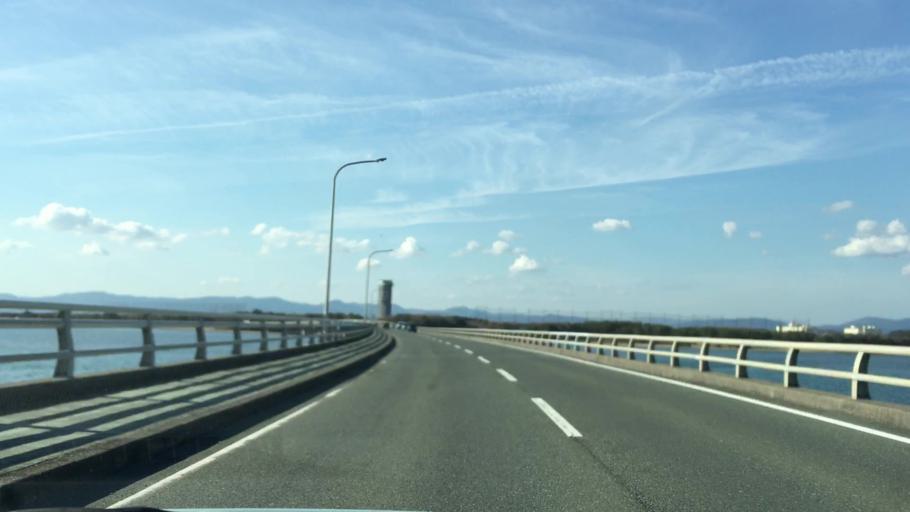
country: JP
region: Shizuoka
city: Kosai-shi
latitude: 34.7085
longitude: 137.6090
